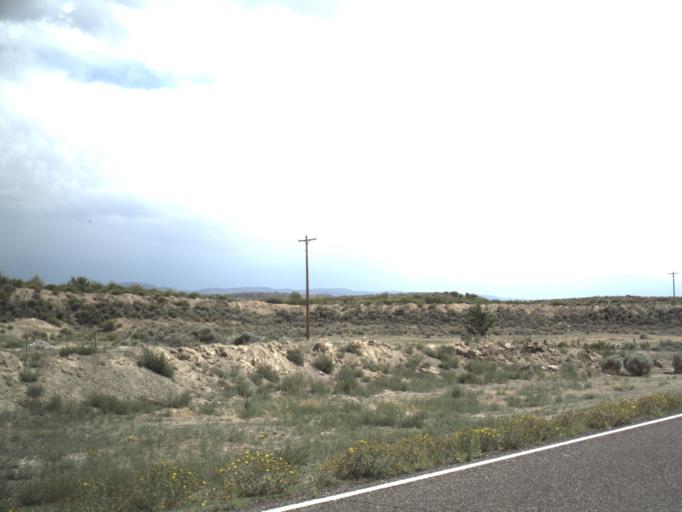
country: US
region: Utah
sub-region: Piute County
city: Junction
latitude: 38.1408
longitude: -111.9979
